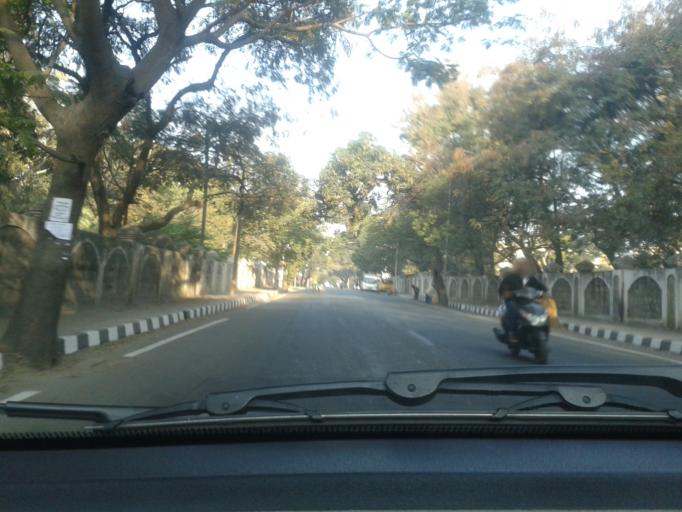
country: IN
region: Karnataka
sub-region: Bangalore Urban
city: Bangalore
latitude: 13.0041
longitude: 77.5953
